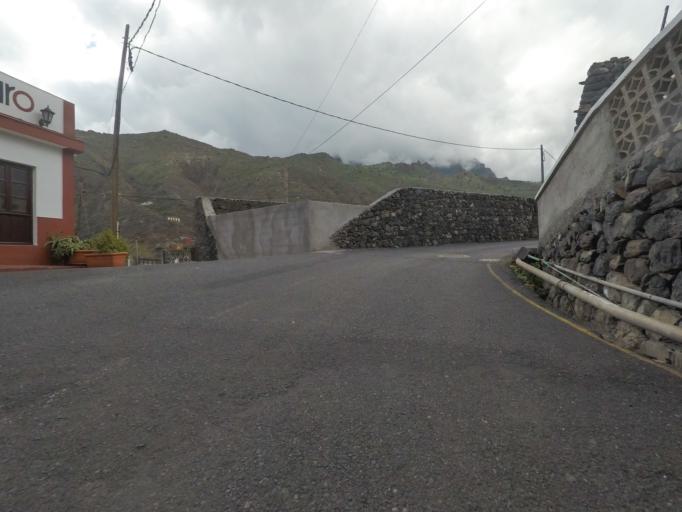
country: ES
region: Canary Islands
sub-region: Provincia de Santa Cruz de Tenerife
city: Hermigua
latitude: 28.1781
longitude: -17.1835
